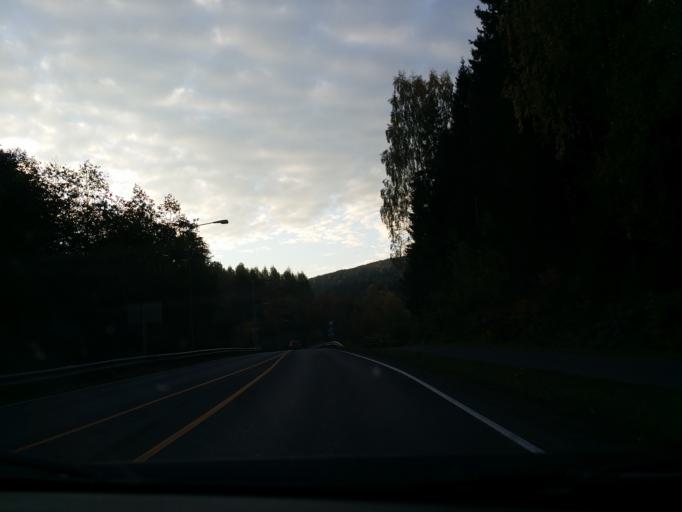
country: NO
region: Akershus
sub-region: Baerum
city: Sandvika
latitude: 59.9460
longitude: 10.5055
